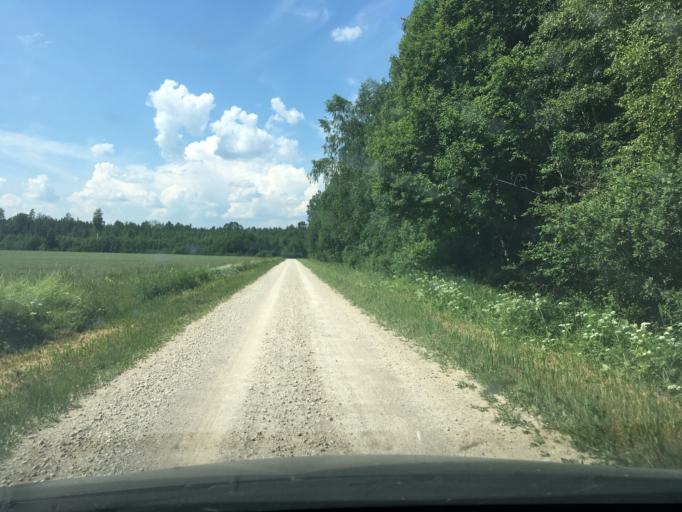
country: EE
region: Raplamaa
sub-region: Maerjamaa vald
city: Marjamaa
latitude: 58.7972
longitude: 24.4574
